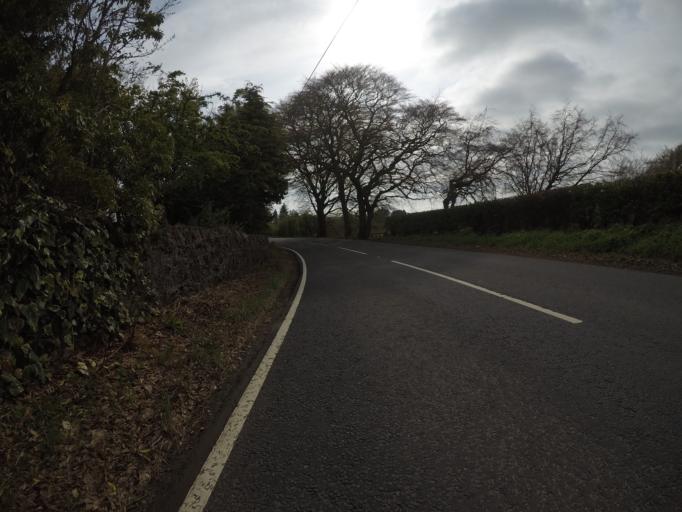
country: GB
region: Scotland
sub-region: East Renfrewshire
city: Newton Mearns
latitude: 55.7515
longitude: -4.3541
